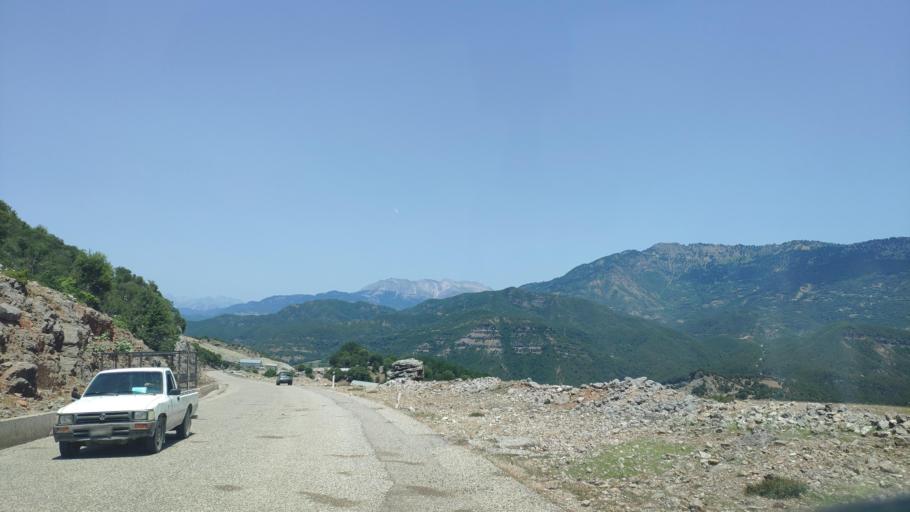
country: GR
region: Thessaly
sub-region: Nomos Kardhitsas
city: Anthiro
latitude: 39.1491
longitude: 21.3870
